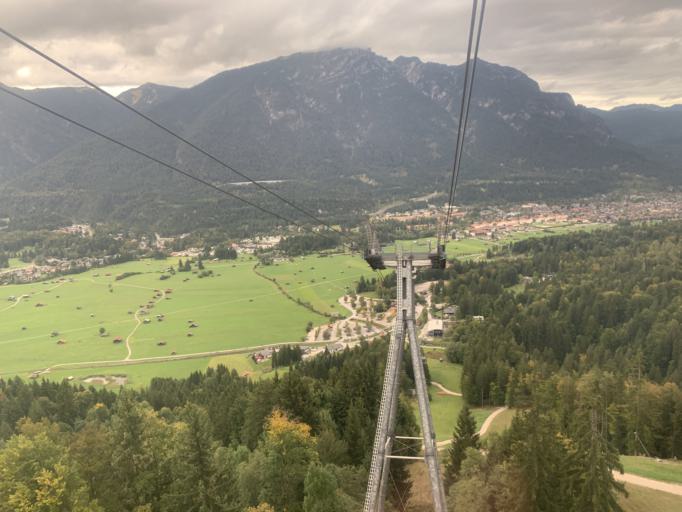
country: DE
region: Bavaria
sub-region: Upper Bavaria
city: Garmisch-Partenkirchen
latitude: 47.4651
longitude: 11.0649
